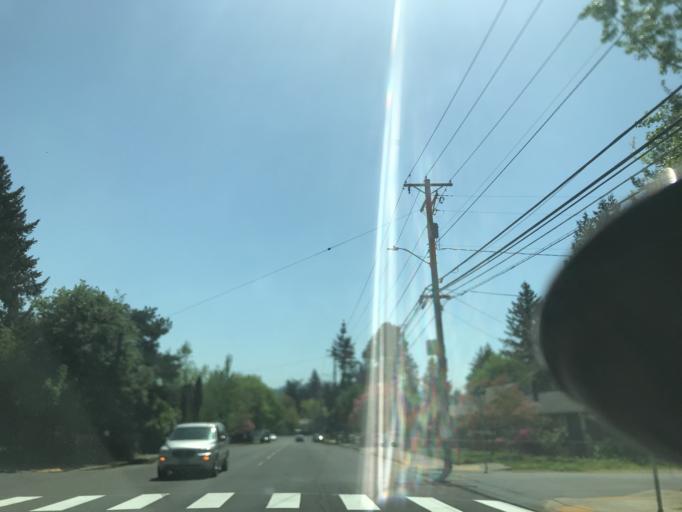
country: US
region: Oregon
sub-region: Multnomah County
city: Lents
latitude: 45.4918
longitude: -122.5480
